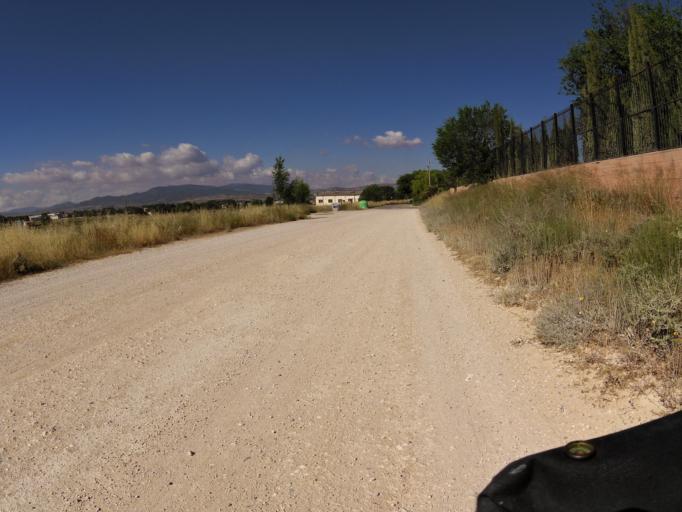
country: ES
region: Valencia
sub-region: Provincia de Alicante
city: Villena
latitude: 38.6314
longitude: -0.8454
